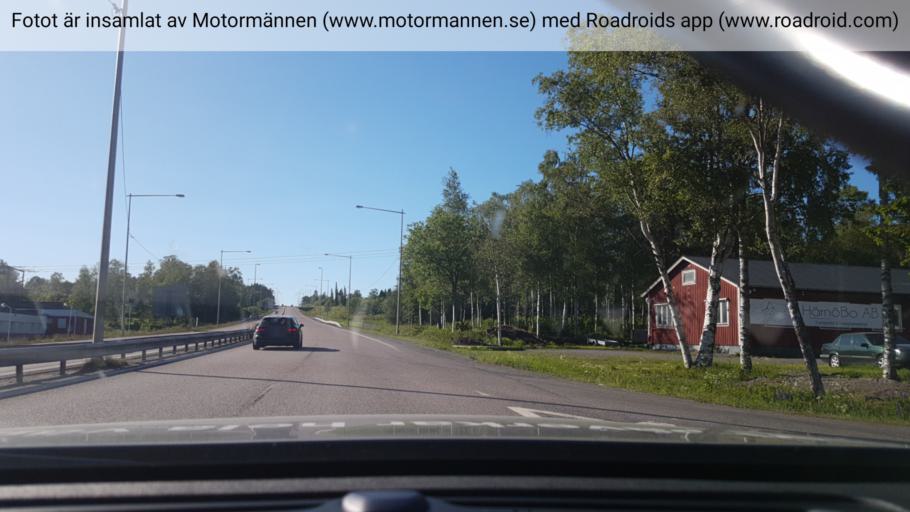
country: SE
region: Vaesternorrland
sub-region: Haernoesands Kommun
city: Haernoesand
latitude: 62.6432
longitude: 17.9103
